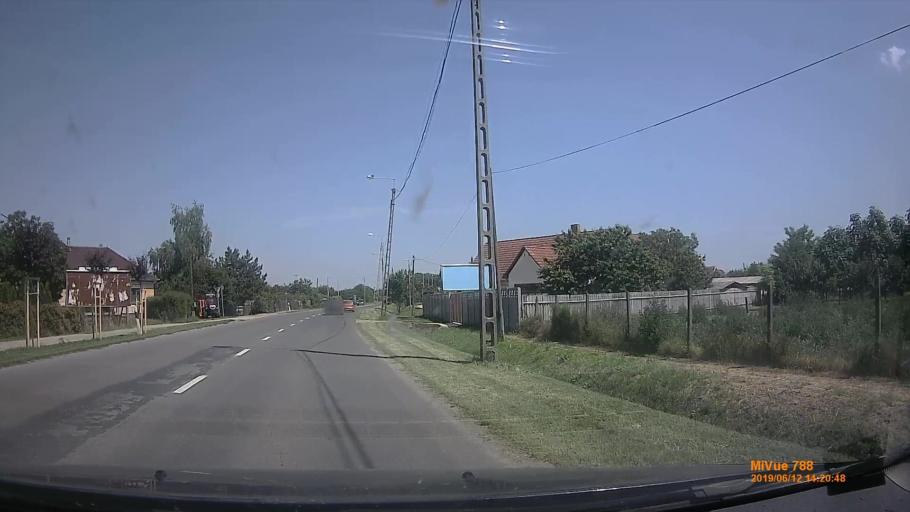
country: HU
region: Csongrad
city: Deszk
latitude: 46.2211
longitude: 20.2502
